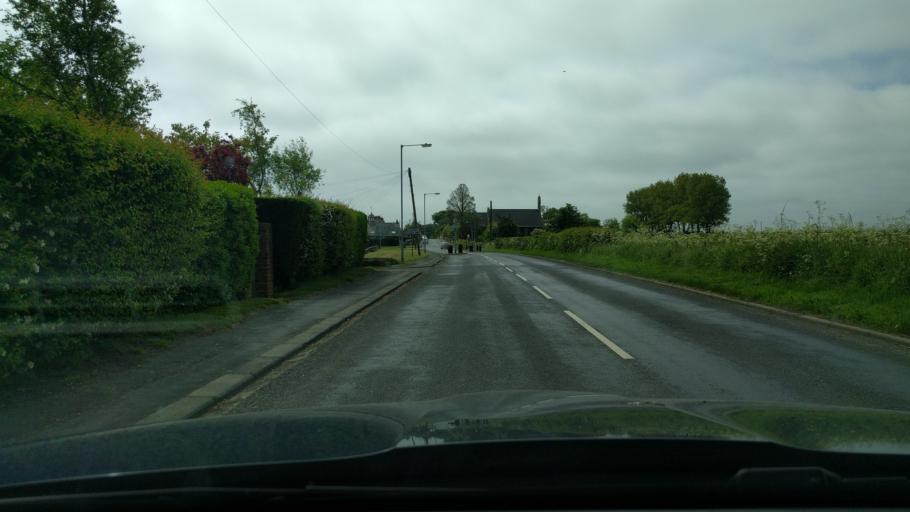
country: GB
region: England
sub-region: Northumberland
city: Acklington
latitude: 55.2941
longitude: -1.6088
